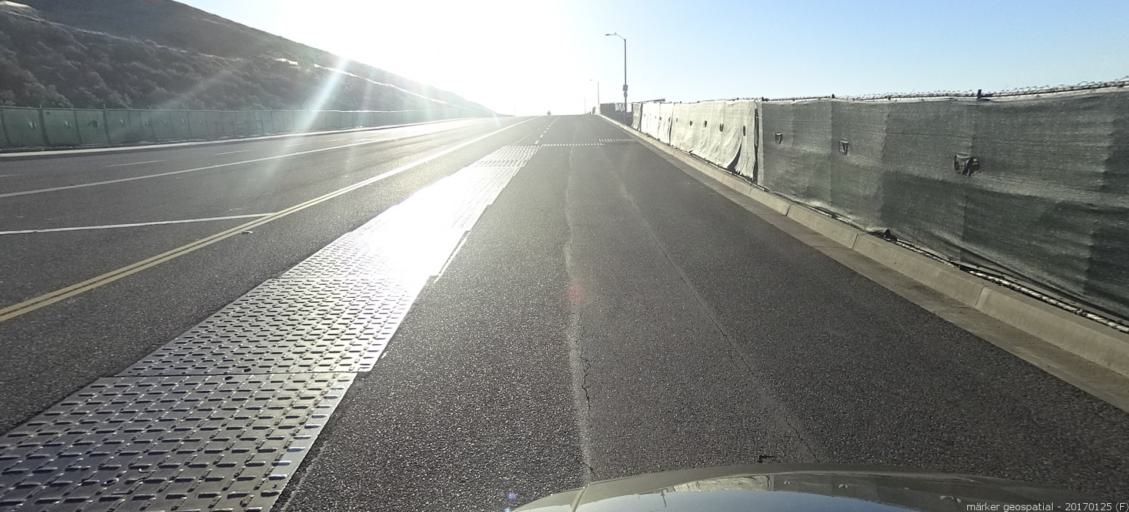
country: US
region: California
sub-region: Orange County
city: Portola Hills
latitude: 33.6733
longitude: -117.6364
